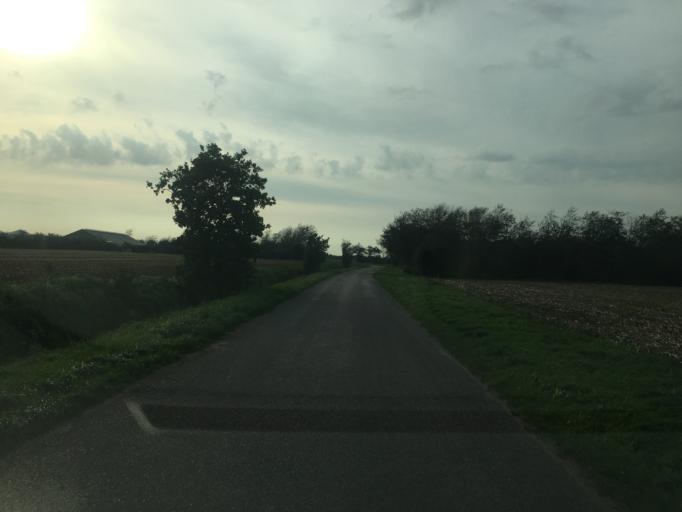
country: DE
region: Schleswig-Holstein
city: Bramstedtlund
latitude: 54.9140
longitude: 9.0683
